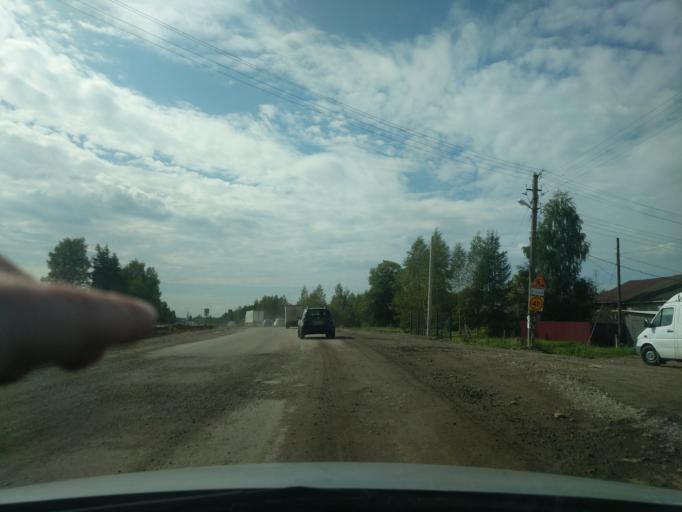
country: RU
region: Kostroma
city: Sudislavl'
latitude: 57.8711
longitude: 41.6477
